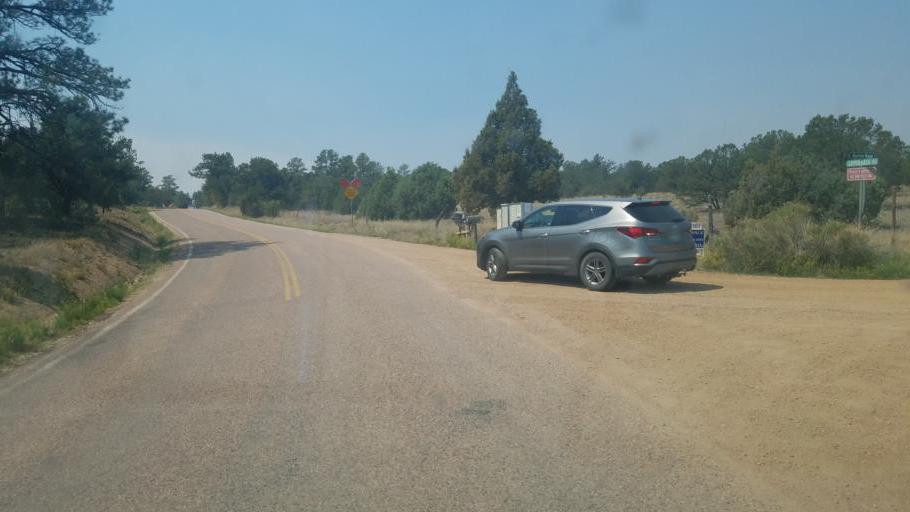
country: US
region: Colorado
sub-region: Custer County
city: Westcliffe
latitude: 38.3598
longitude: -105.4719
